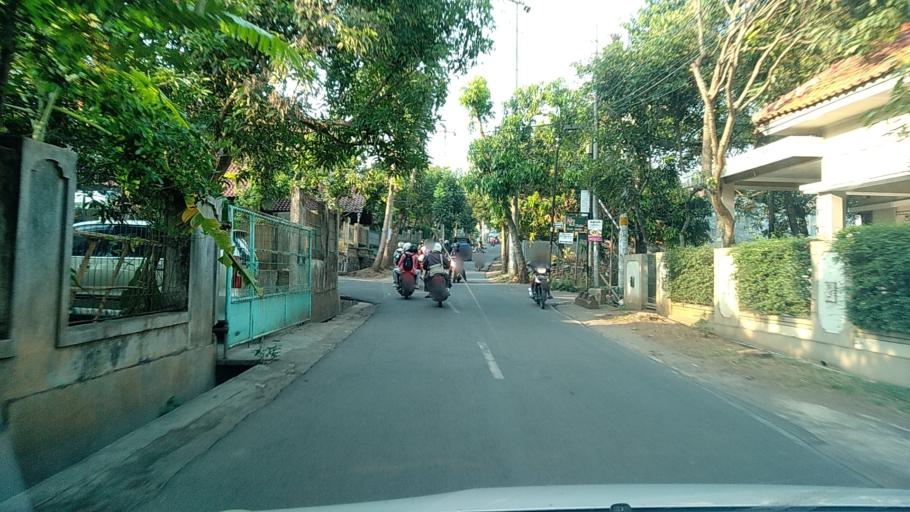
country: ID
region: Central Java
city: Semarang
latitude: -7.0665
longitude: 110.4401
